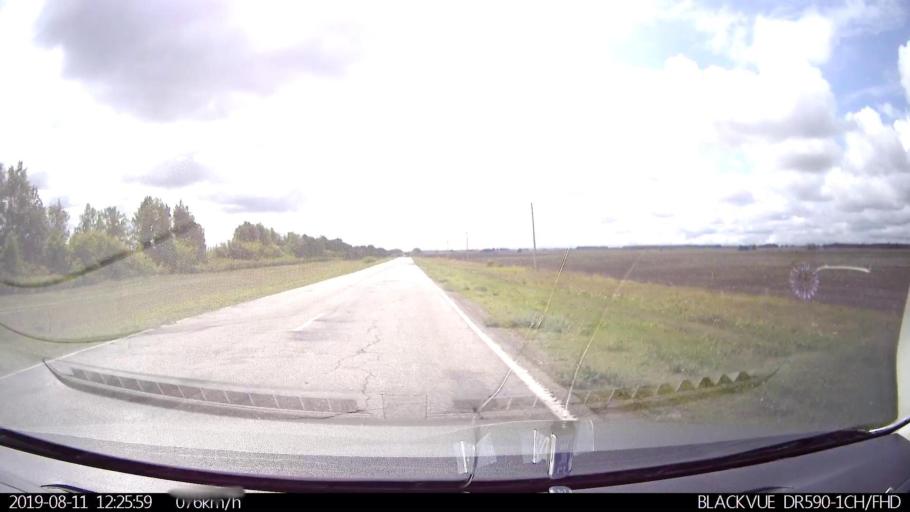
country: RU
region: Ulyanovsk
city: Ignatovka
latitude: 53.8683
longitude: 47.9346
